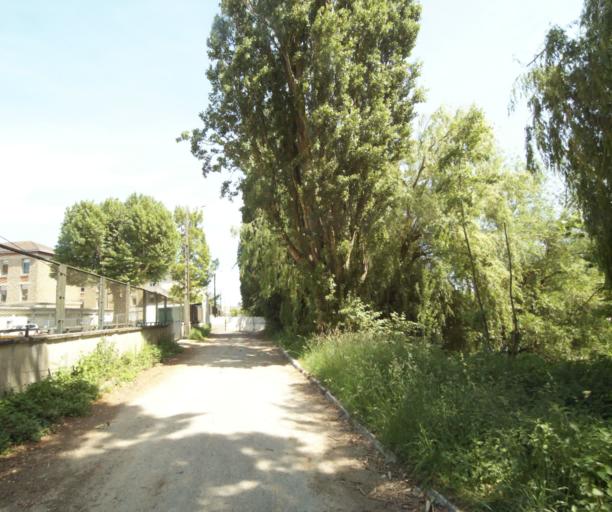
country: FR
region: Champagne-Ardenne
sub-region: Departement des Ardennes
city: Prix-les-Mezieres
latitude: 49.7617
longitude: 4.6978
